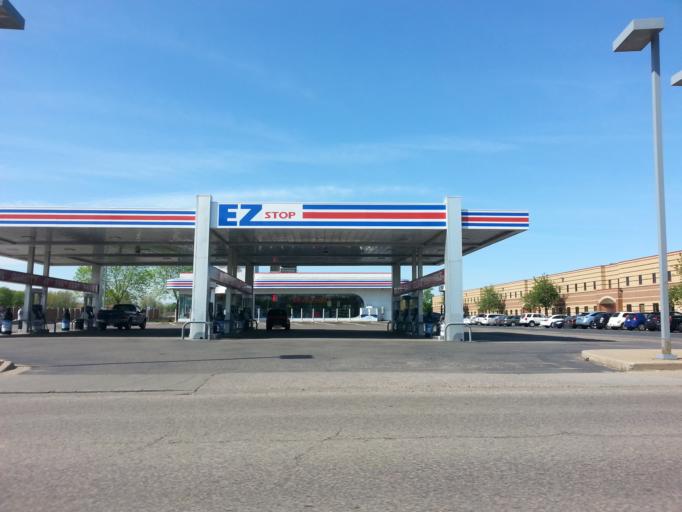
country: US
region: Minnesota
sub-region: Hennepin County
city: Saint Anthony
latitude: 44.9987
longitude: -93.2362
